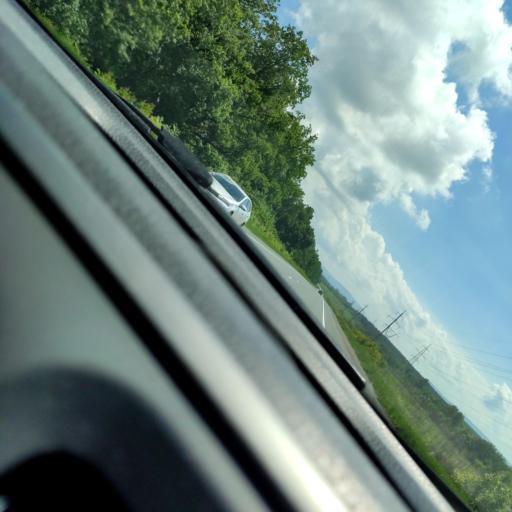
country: RU
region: Samara
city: Bogatyr'
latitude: 53.4993
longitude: 49.9548
